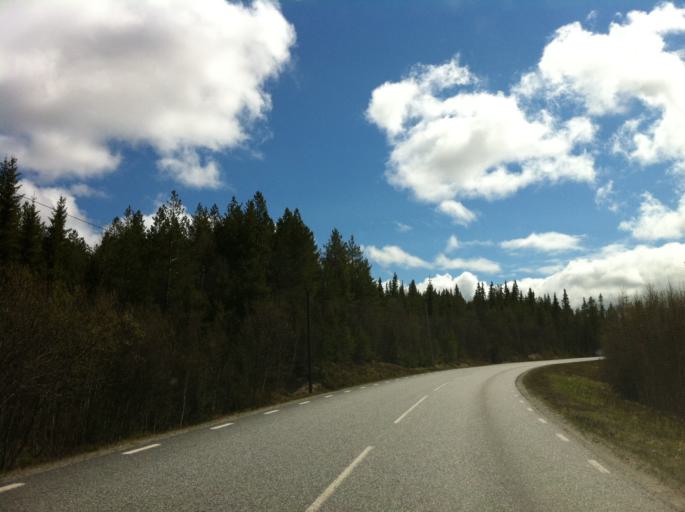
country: SE
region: Jaemtland
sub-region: Are Kommun
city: Are
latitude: 62.5828
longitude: 12.5582
